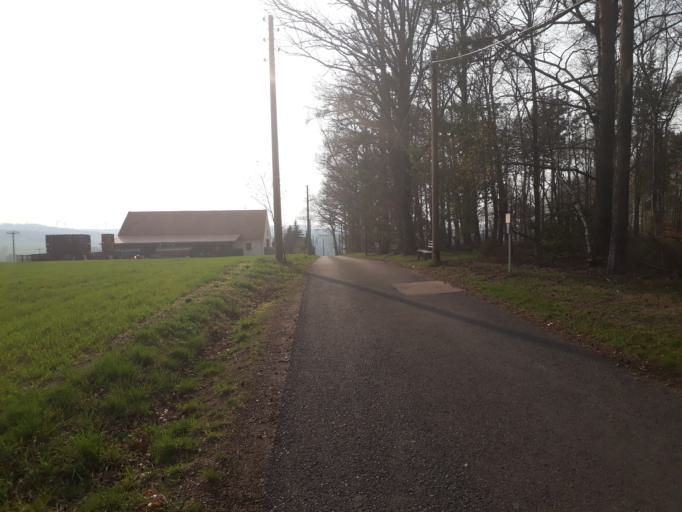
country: DE
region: Saxony
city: Reinhardtsgrimma
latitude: 50.8931
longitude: 13.7710
